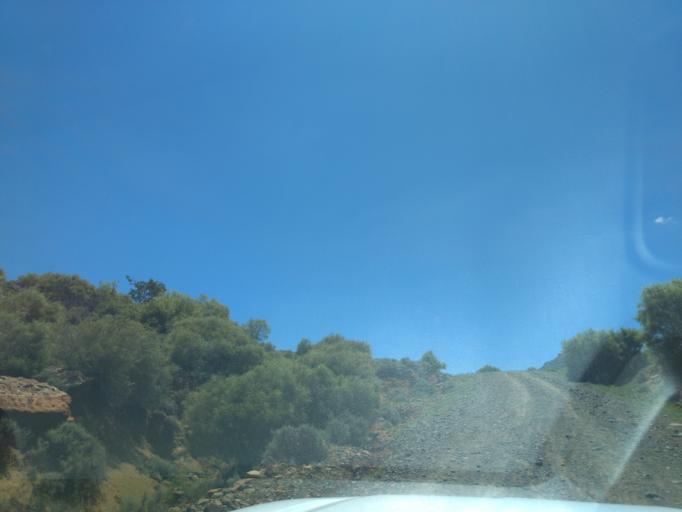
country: LS
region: Maseru
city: Maseru
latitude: -29.4777
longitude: 27.3743
